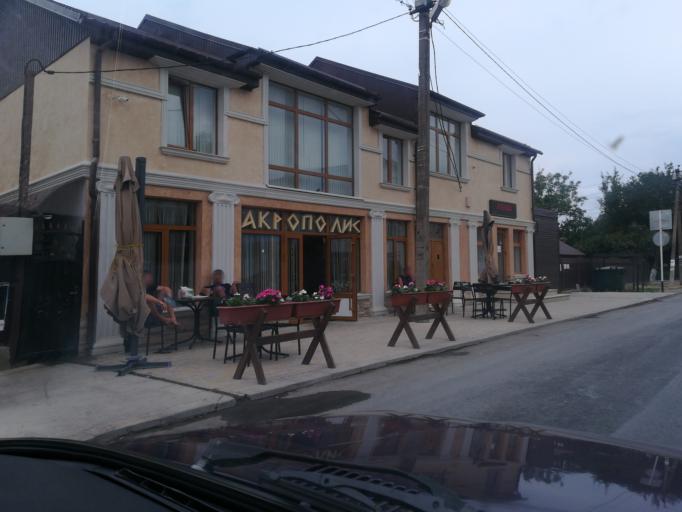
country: RU
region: Krasnodarskiy
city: Vityazevo
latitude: 45.0046
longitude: 37.2852
